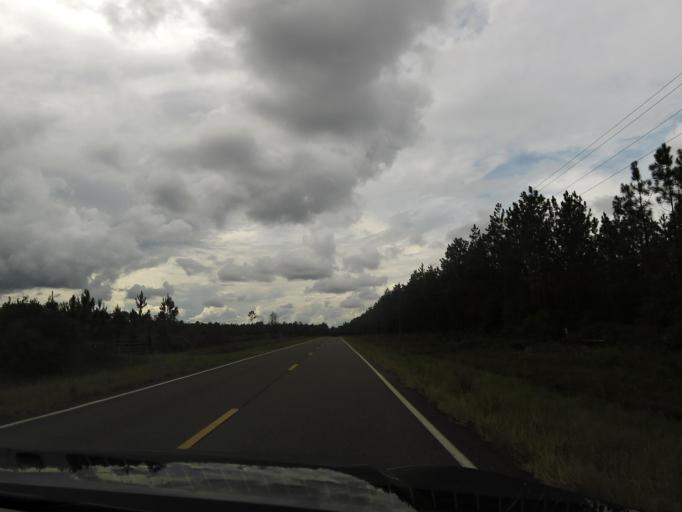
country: US
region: Florida
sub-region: Baker County
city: Macclenny
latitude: 30.4992
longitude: -82.2051
